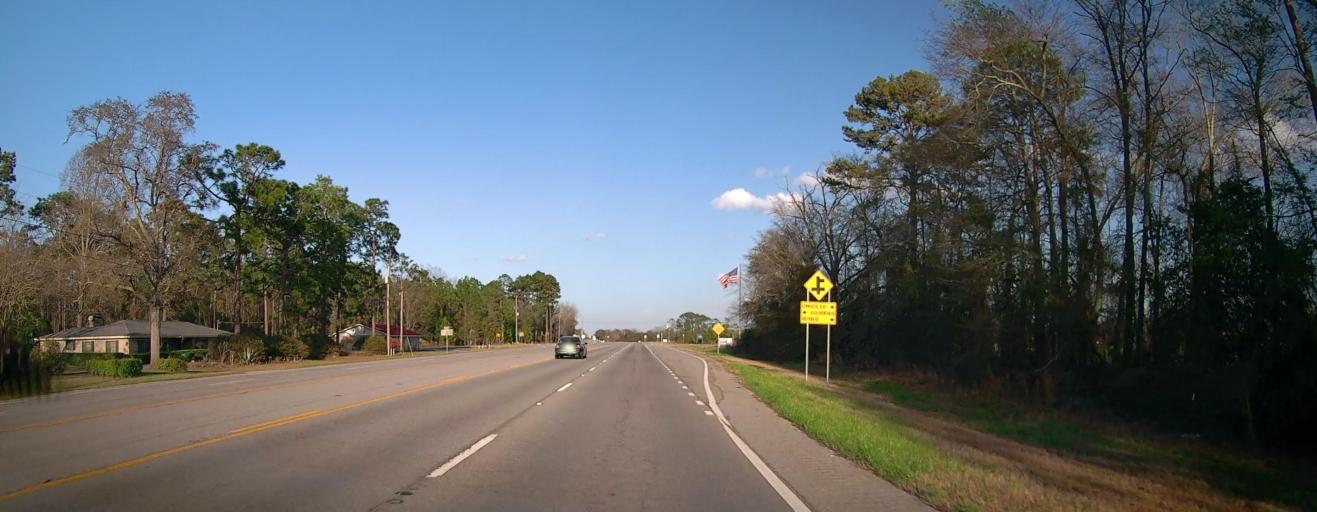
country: US
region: Georgia
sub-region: Evans County
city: Claxton
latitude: 32.1526
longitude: -81.9563
